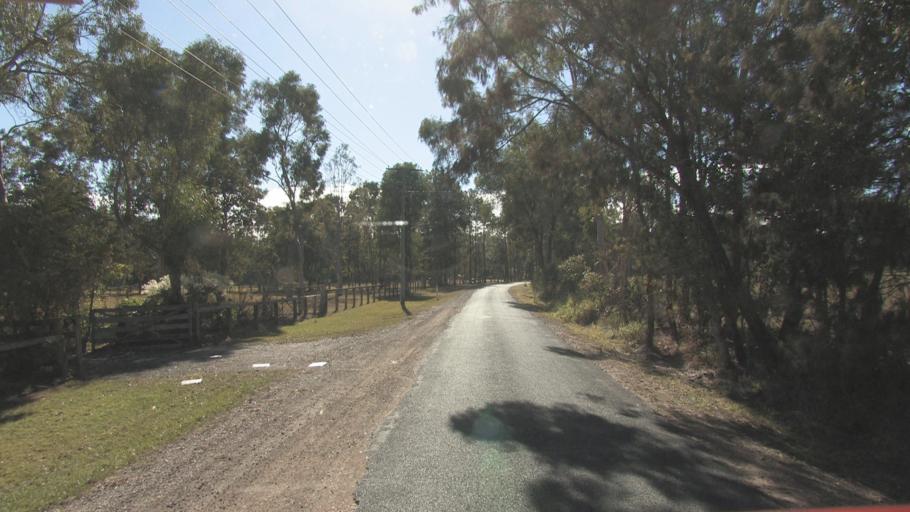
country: AU
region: Queensland
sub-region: Logan
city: Chambers Flat
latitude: -27.7874
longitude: 153.0683
